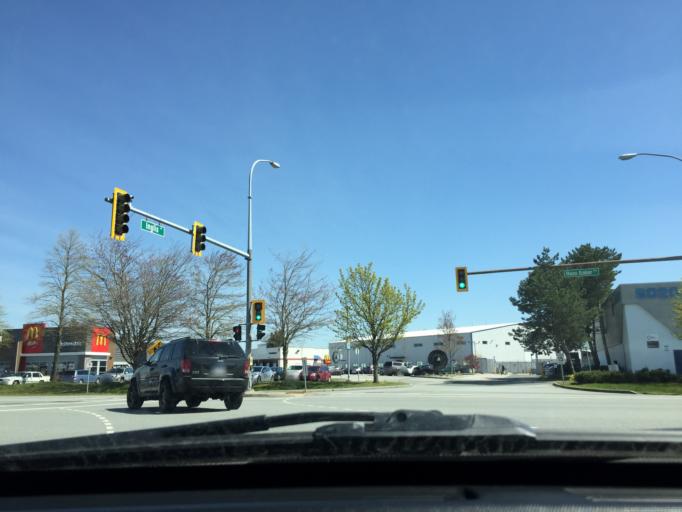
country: CA
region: British Columbia
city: Richmond
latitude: 49.1798
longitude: -123.1537
